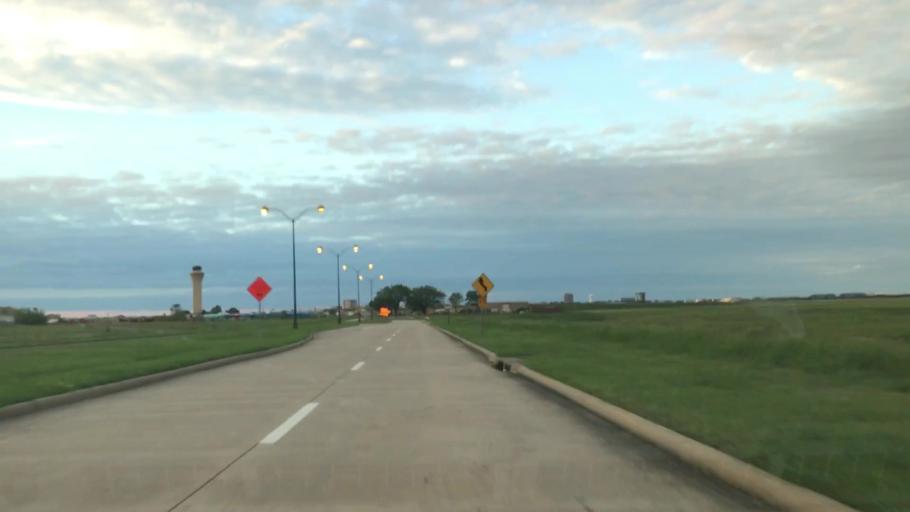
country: US
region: Texas
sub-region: Dallas County
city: Coppell
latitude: 32.8861
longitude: -97.0156
